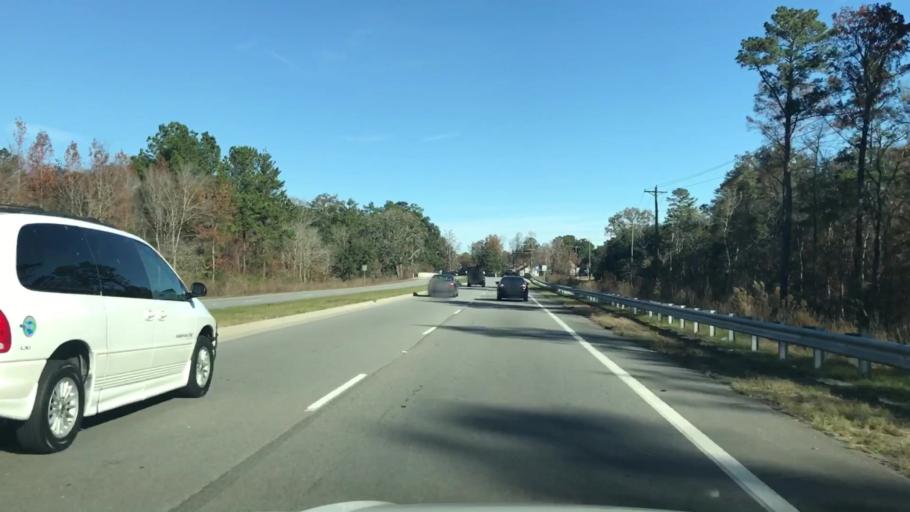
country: US
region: South Carolina
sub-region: Dorchester County
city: Centerville
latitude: 32.9563
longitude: -80.2012
